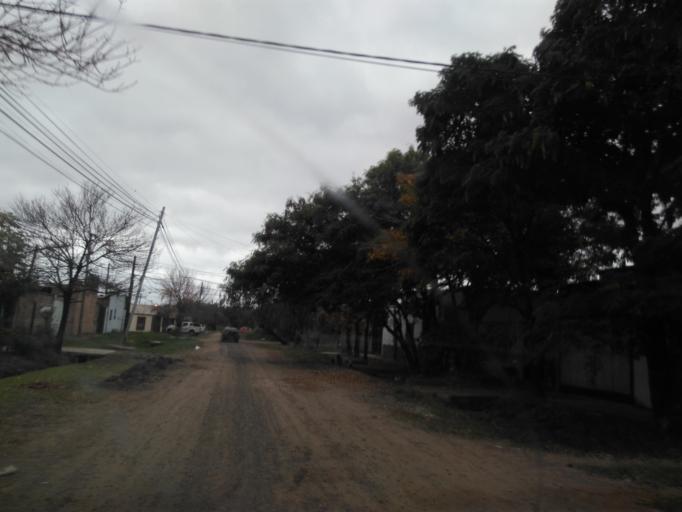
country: AR
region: Chaco
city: Fontana
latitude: -27.4519
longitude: -59.0338
